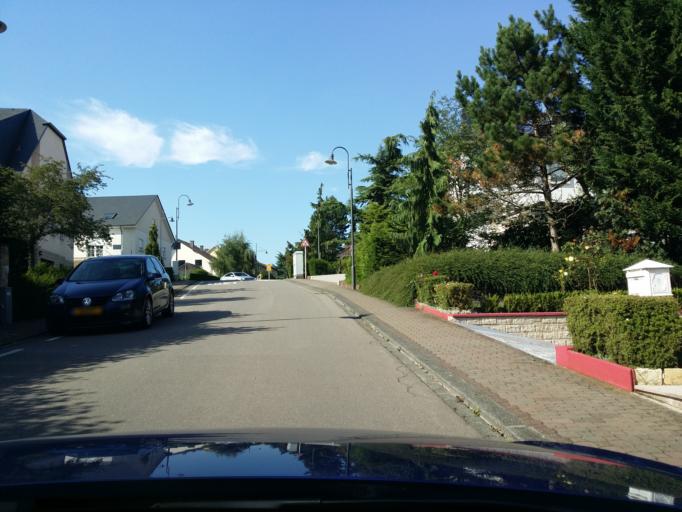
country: LU
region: Luxembourg
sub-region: Canton de Luxembourg
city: Bertrange
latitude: 49.6177
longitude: 6.0584
